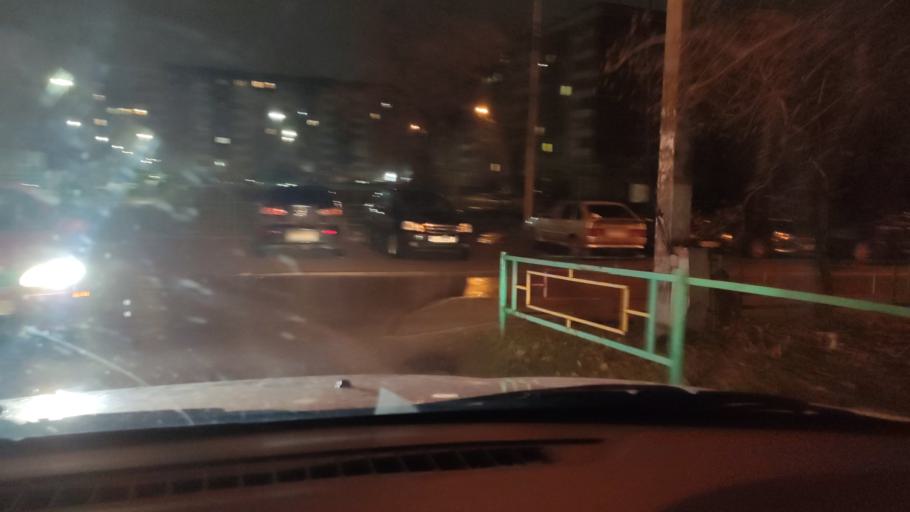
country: RU
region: Perm
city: Kondratovo
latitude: 57.9980
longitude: 56.1404
